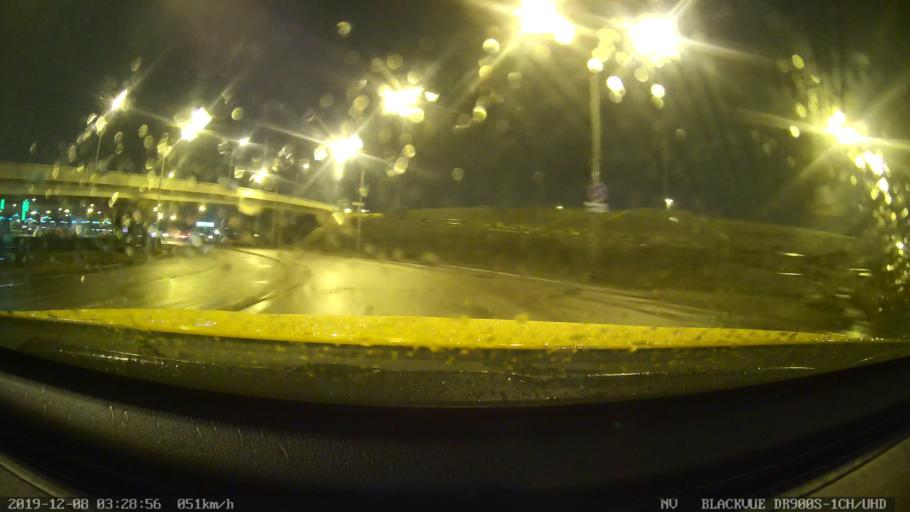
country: RU
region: Moskovskaya
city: Mosrentgen
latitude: 55.6254
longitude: 37.4263
